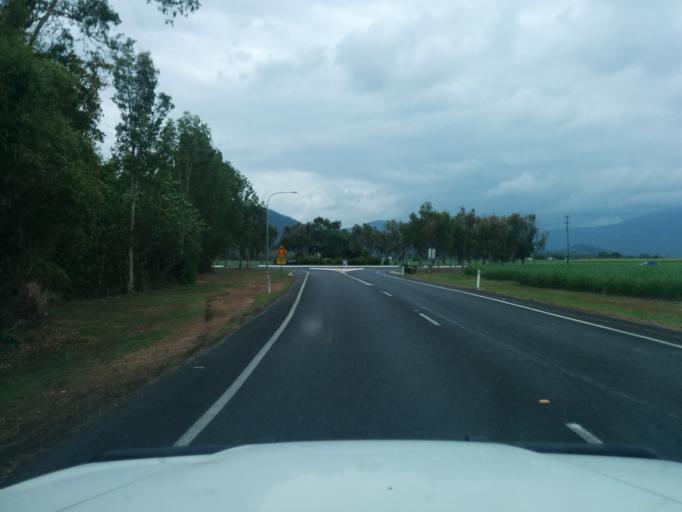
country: AU
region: Queensland
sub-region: Cairns
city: Redlynch
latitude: -16.8498
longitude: 145.7335
